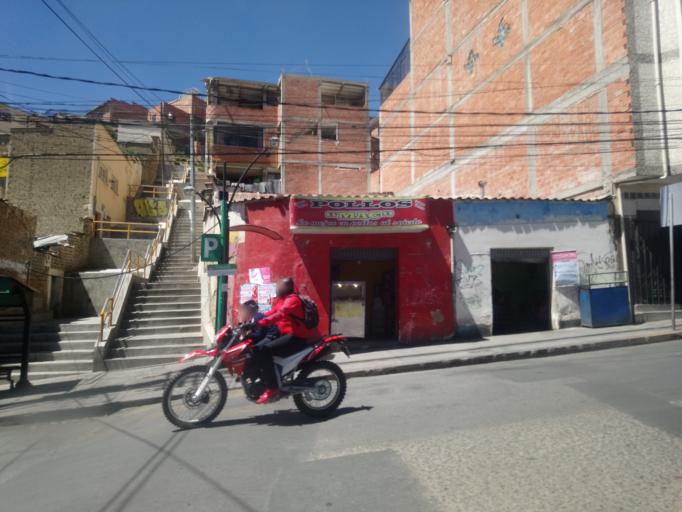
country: BO
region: La Paz
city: La Paz
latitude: -16.4973
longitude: -68.1087
